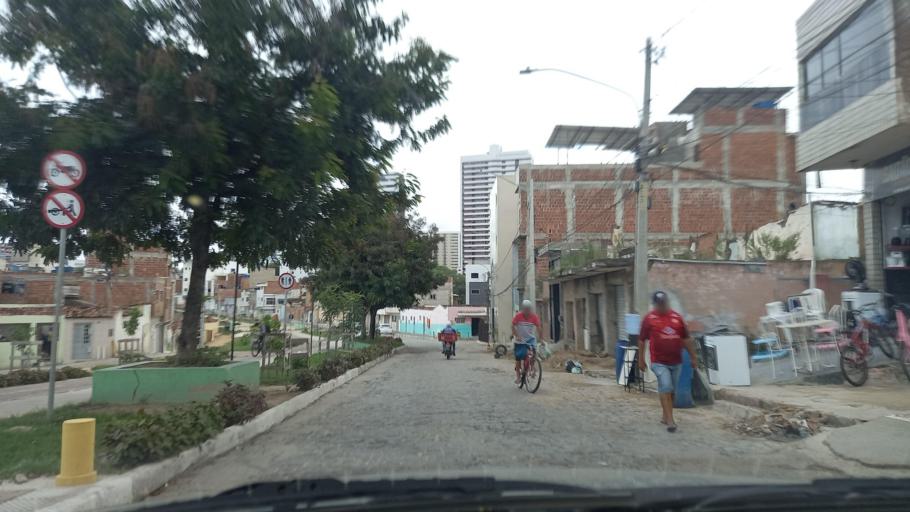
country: BR
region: Pernambuco
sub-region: Caruaru
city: Caruaru
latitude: -8.2794
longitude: -35.9643
